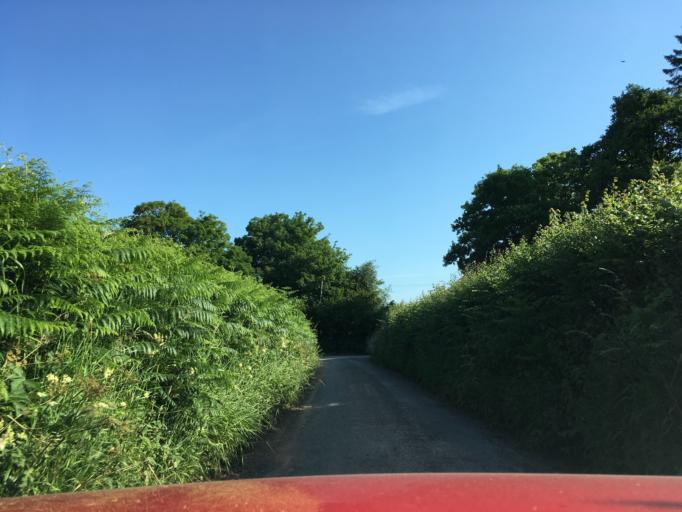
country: GB
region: England
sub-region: Gloucestershire
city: Berkeley
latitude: 51.7573
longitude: -2.4648
